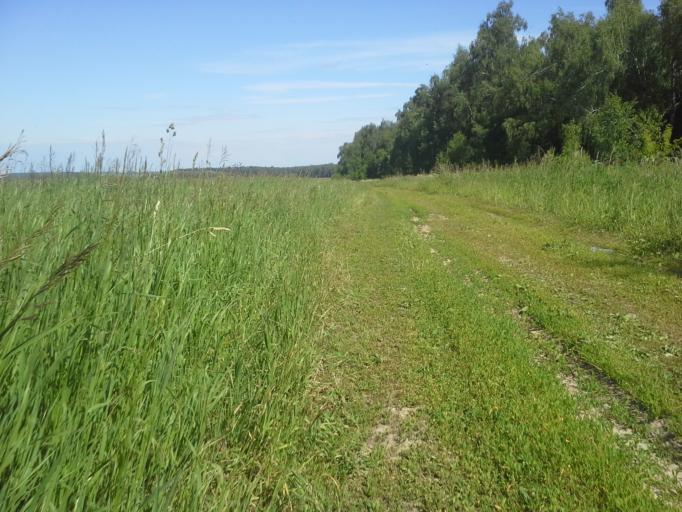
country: RU
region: Moskovskaya
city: Dubrovitsy
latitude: 55.4699
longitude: 37.4250
